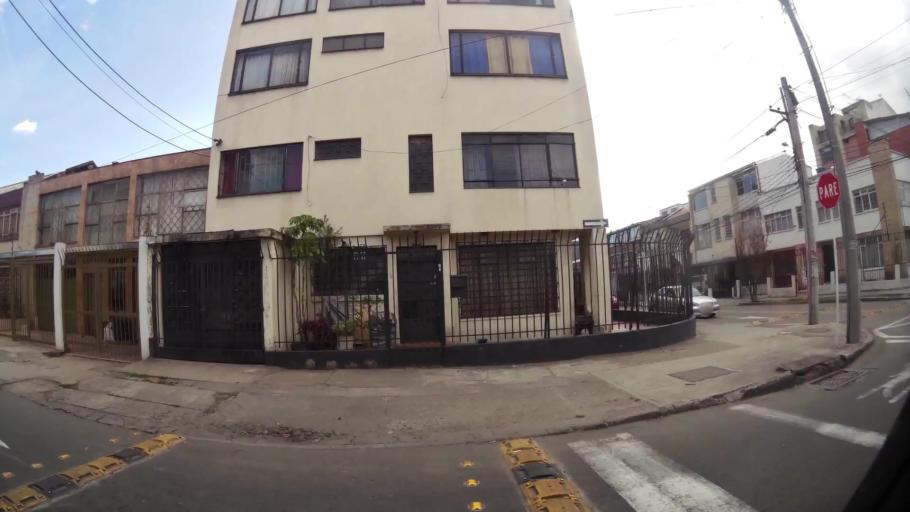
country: CO
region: Bogota D.C.
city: Bogota
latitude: 4.6490
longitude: -74.0743
